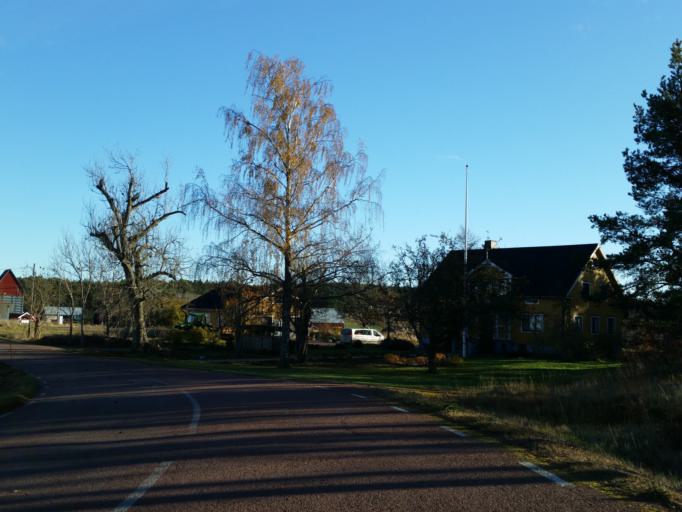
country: AX
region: Alands landsbygd
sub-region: Finstroem
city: Finstroem
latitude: 60.3456
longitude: 19.9560
